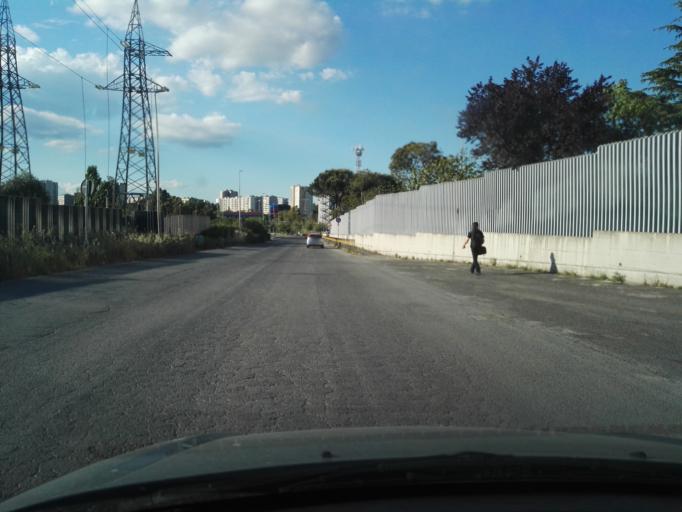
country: IT
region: Latium
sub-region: Citta metropolitana di Roma Capitale
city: Selcetta
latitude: 41.7990
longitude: 12.4820
